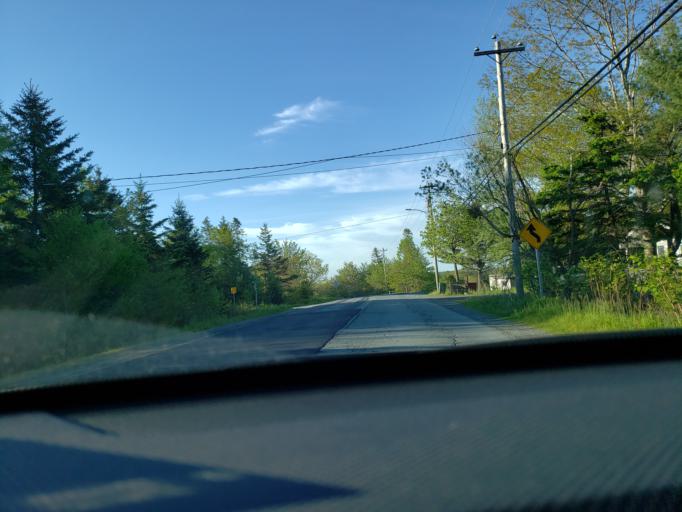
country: CA
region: Nova Scotia
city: Cole Harbour
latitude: 44.7215
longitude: -63.3997
